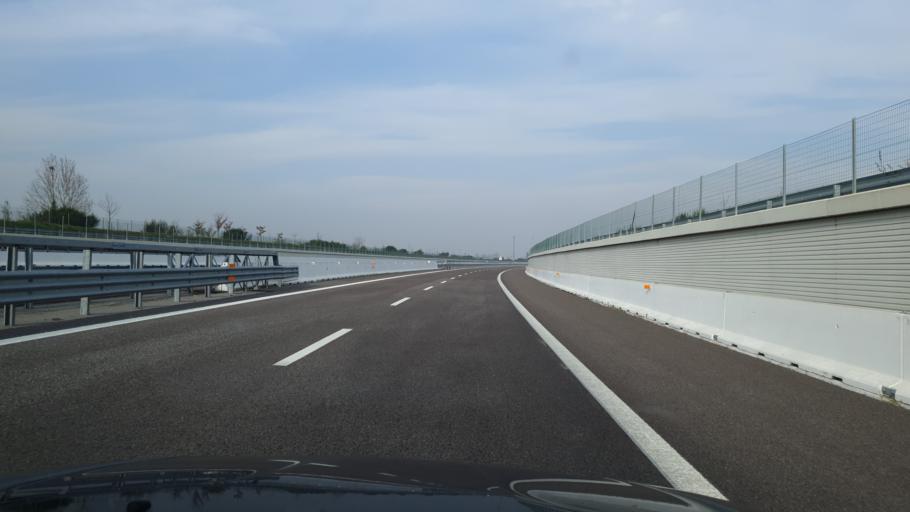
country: IT
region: Veneto
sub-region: Provincia di Vicenza
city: Agugliaro
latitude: 45.3193
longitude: 11.5750
